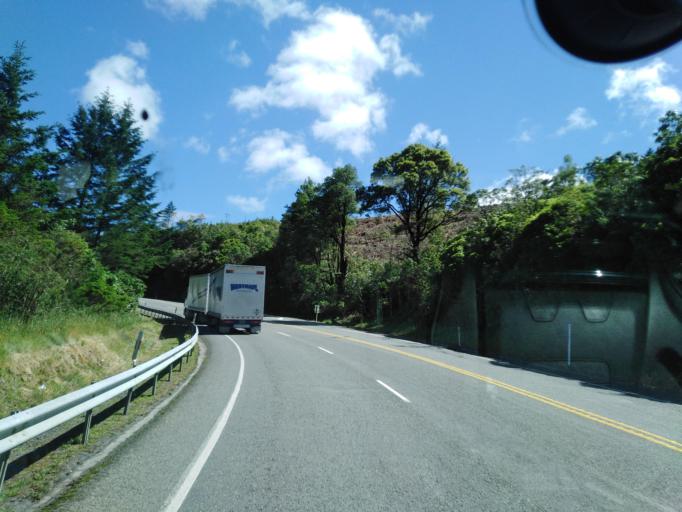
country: NZ
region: Nelson
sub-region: Nelson City
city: Nelson
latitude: -41.1926
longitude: 173.5573
